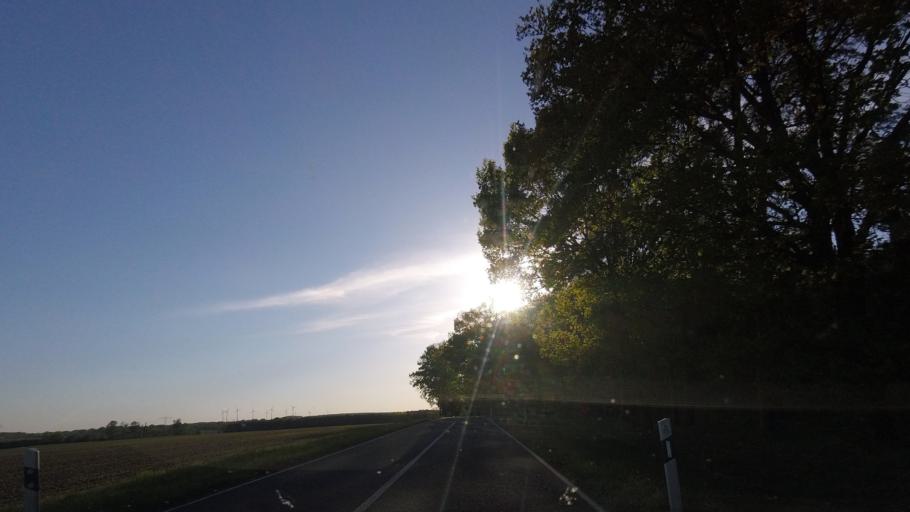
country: DE
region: Brandenburg
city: Luckenwalde
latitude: 51.9858
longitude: 13.1973
